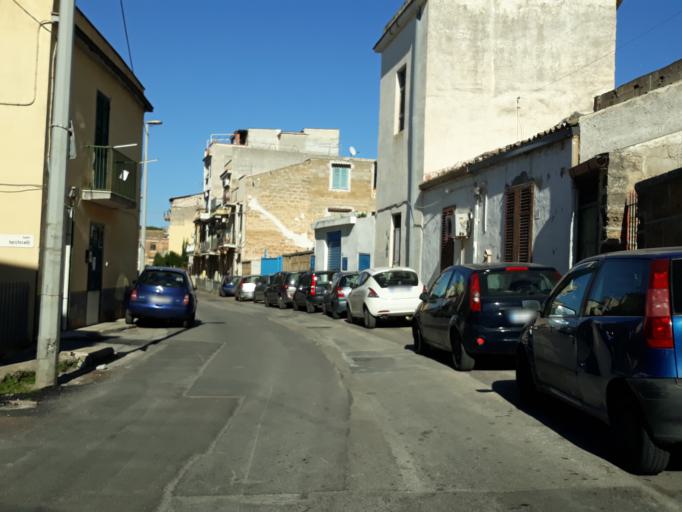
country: IT
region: Sicily
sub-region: Palermo
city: Ciaculli
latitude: 38.0790
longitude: 13.3717
